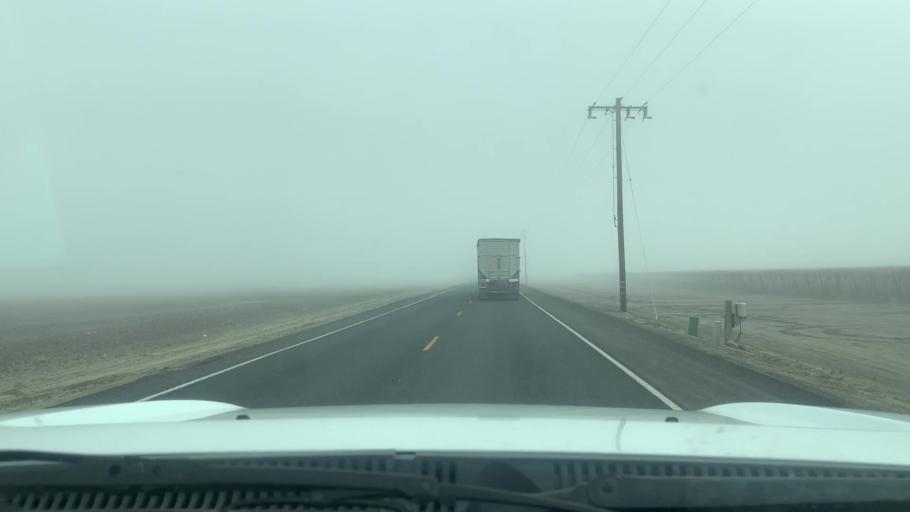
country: US
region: California
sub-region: Kern County
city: Buttonwillow
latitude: 35.4996
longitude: -119.5701
